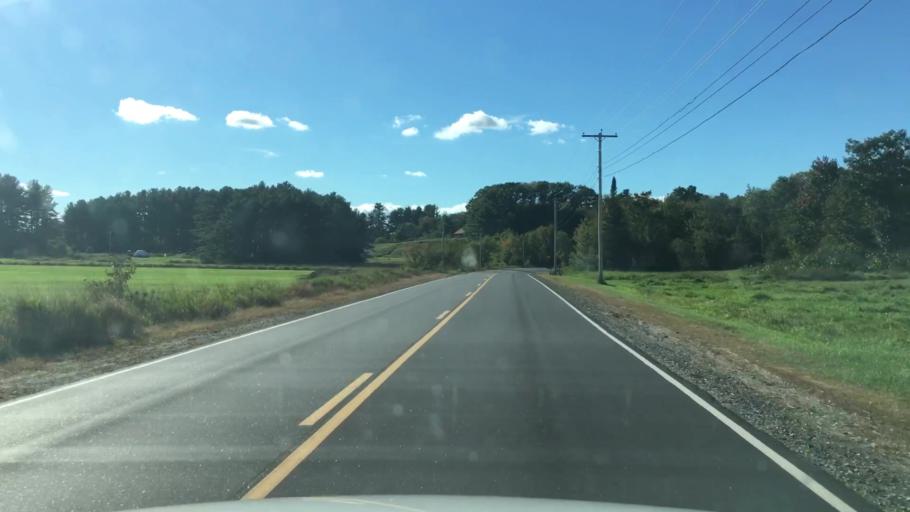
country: US
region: Maine
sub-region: Androscoggin County
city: Lisbon
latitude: 44.0734
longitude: -70.0956
